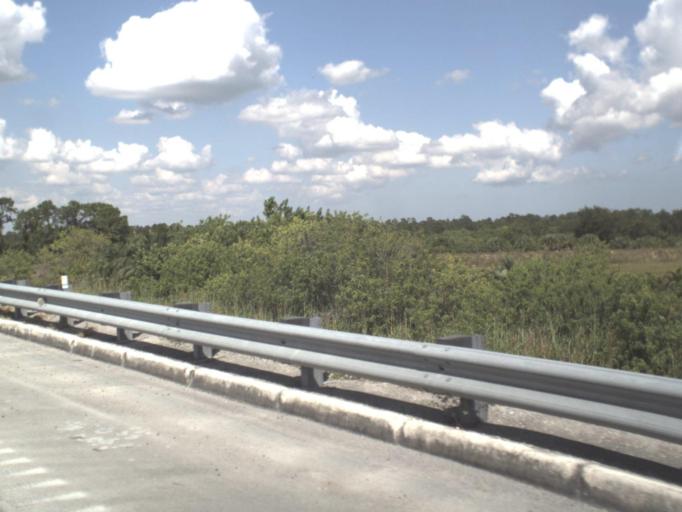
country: US
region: Florida
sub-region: Saint Lucie County
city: Lakewood Park
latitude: 27.4687
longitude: -80.4414
